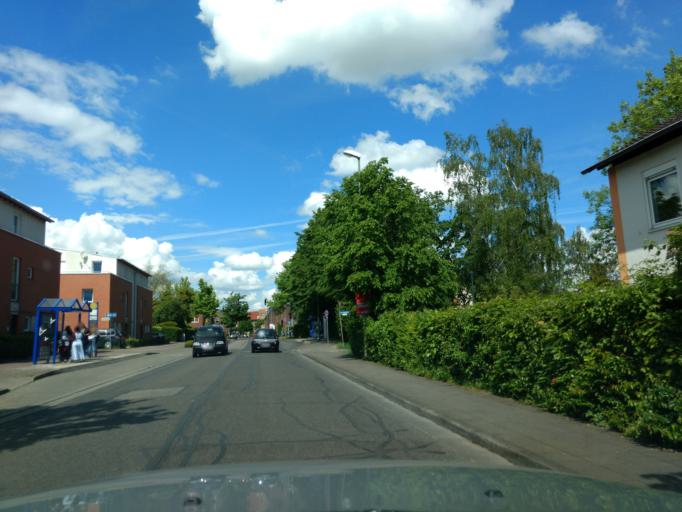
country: DE
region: North Rhine-Westphalia
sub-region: Regierungsbezirk Dusseldorf
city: Meerbusch
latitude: 51.2409
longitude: 6.6967
